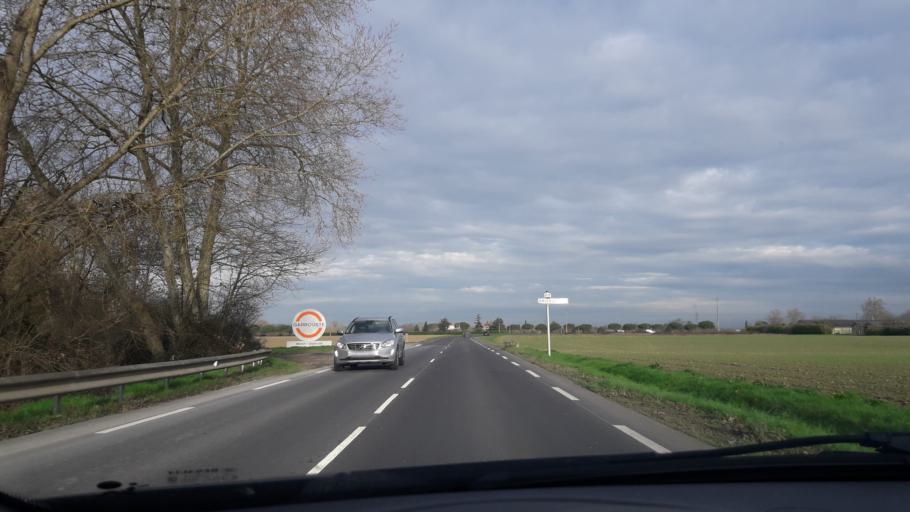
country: FR
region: Midi-Pyrenees
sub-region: Departement de la Haute-Garonne
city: Ondes
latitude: 43.7817
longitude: 1.3044
